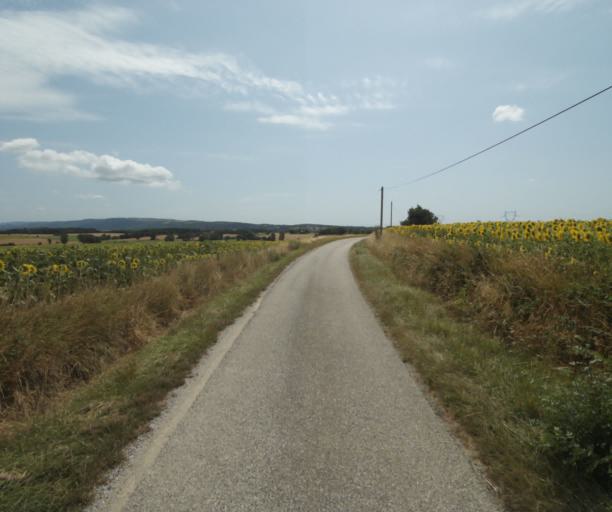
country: FR
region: Midi-Pyrenees
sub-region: Departement de la Haute-Garonne
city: Saint-Felix-Lauragais
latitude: 43.4157
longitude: 1.9110
